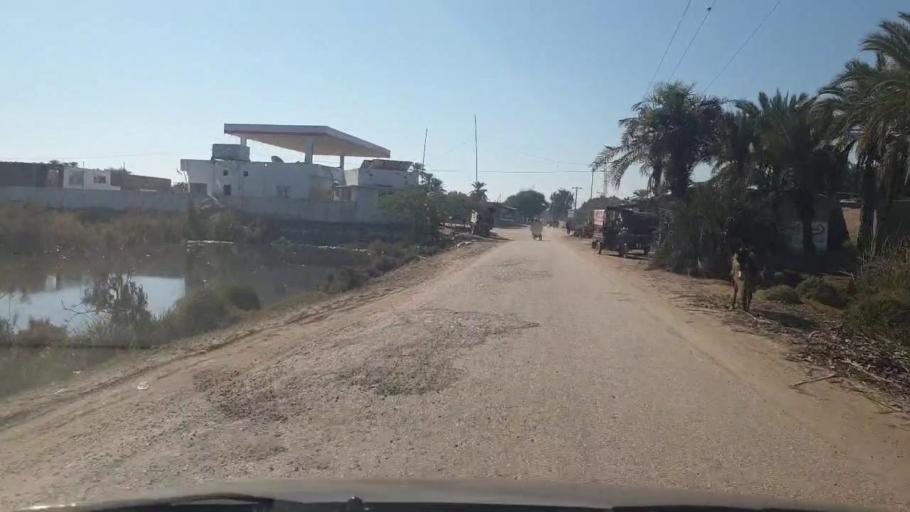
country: PK
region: Sindh
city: Bozdar
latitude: 27.0755
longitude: 68.6157
